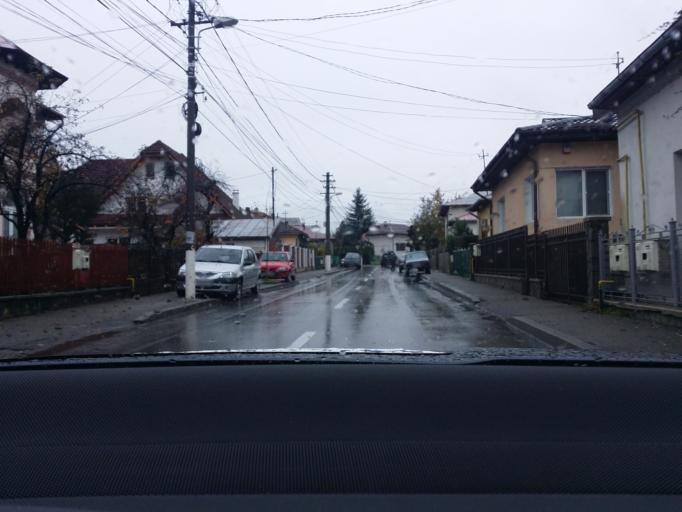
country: RO
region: Prahova
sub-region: Municipiul Campina
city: Campina
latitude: 45.1252
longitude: 25.7286
